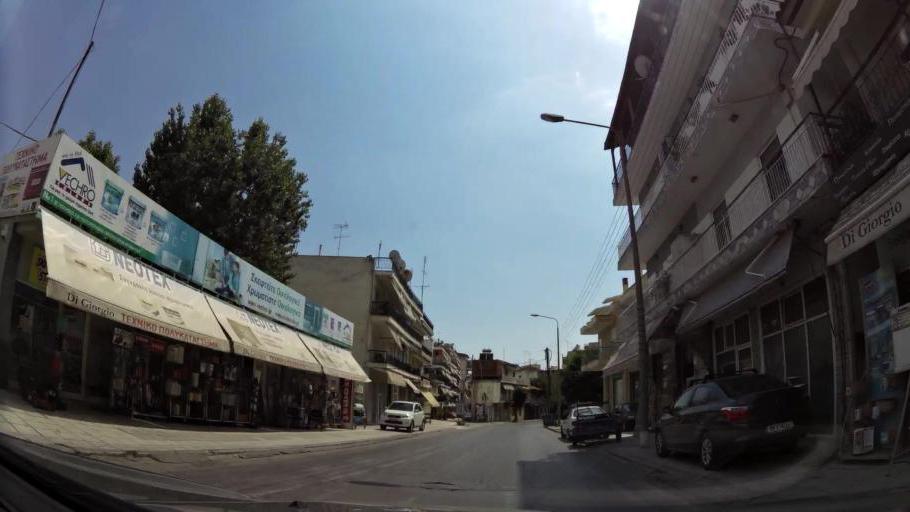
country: GR
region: Central Macedonia
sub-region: Nomos Thessalonikis
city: Stavroupoli
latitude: 40.6720
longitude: 22.9412
